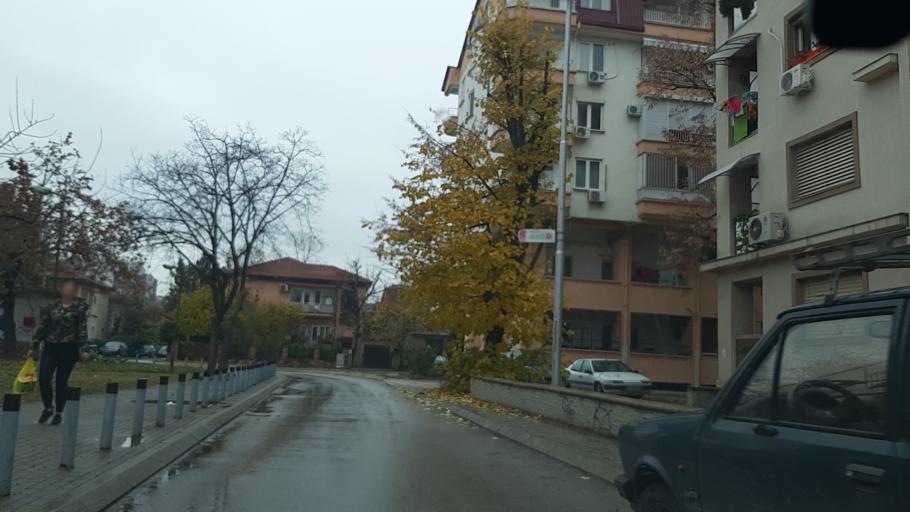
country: MK
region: Karpos
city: Skopje
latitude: 41.9873
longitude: 21.4482
